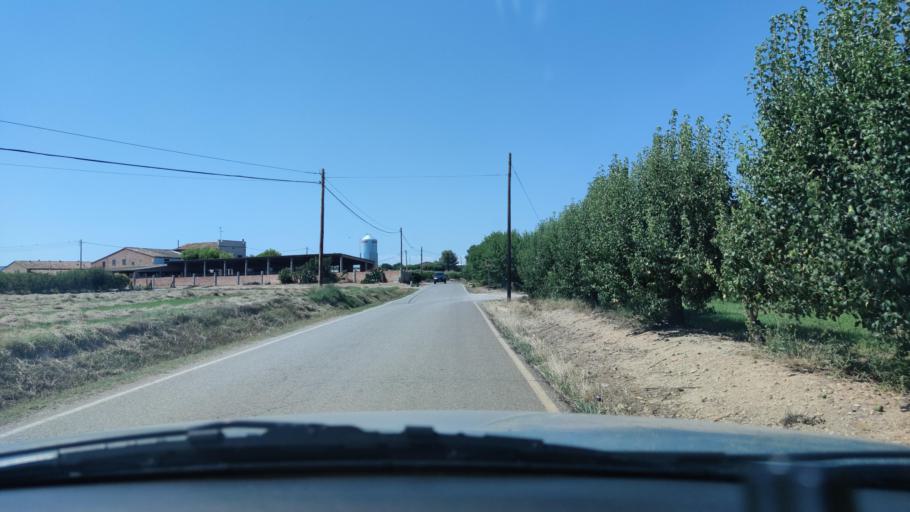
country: ES
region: Catalonia
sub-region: Provincia de Lleida
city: Torrefarrera
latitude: 41.6505
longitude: 0.6236
